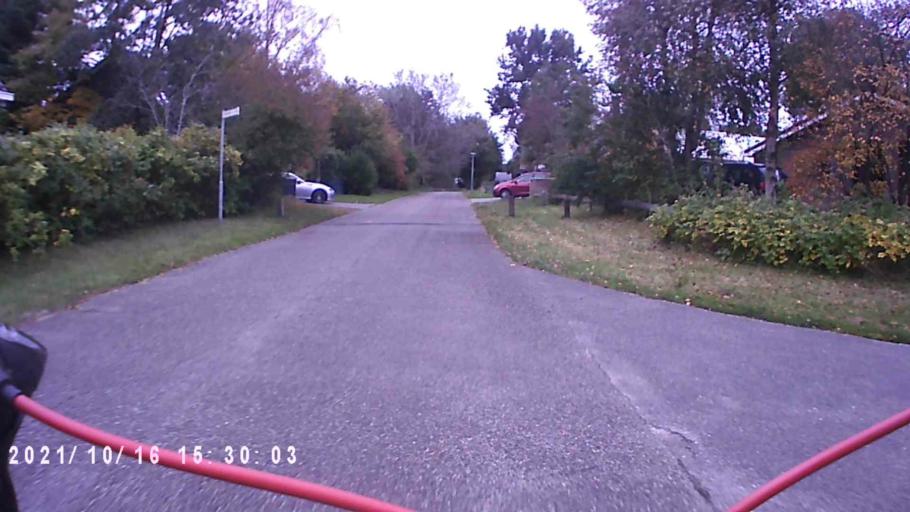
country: NL
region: Friesland
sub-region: Gemeente Dongeradeel
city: Anjum
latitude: 53.4050
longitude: 6.2211
